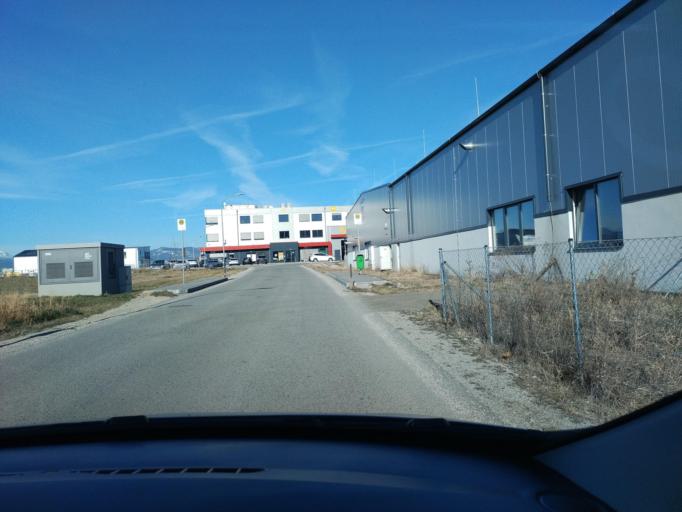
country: AT
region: Lower Austria
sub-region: Politischer Bezirk Wiener Neustadt
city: Lanzenkirchen
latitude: 47.7561
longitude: 16.2489
